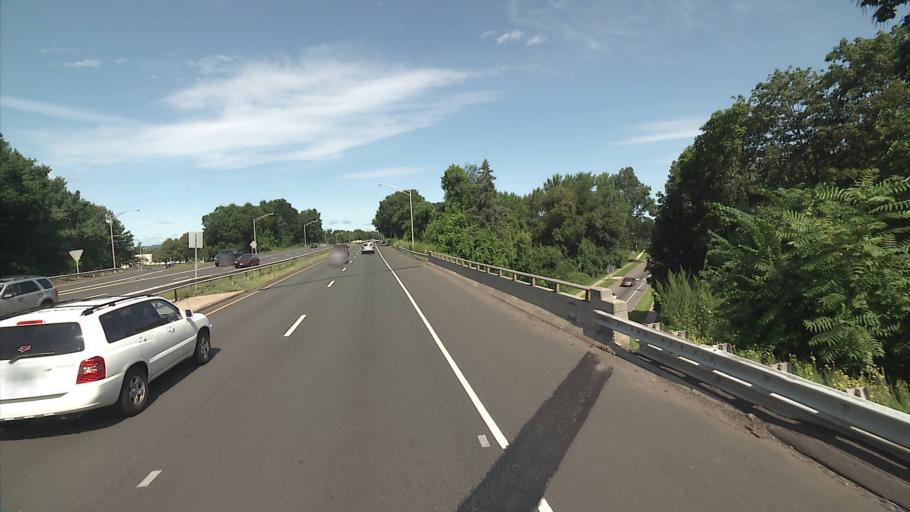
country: US
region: Connecticut
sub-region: Hartford County
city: Wethersfield
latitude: 41.7407
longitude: -72.6316
